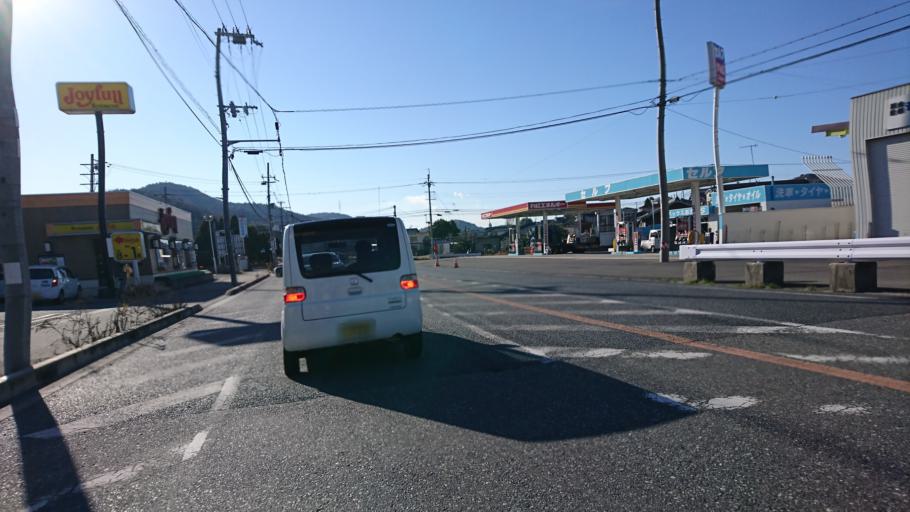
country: JP
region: Hyogo
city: Kakogawacho-honmachi
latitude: 34.8153
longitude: 134.8356
